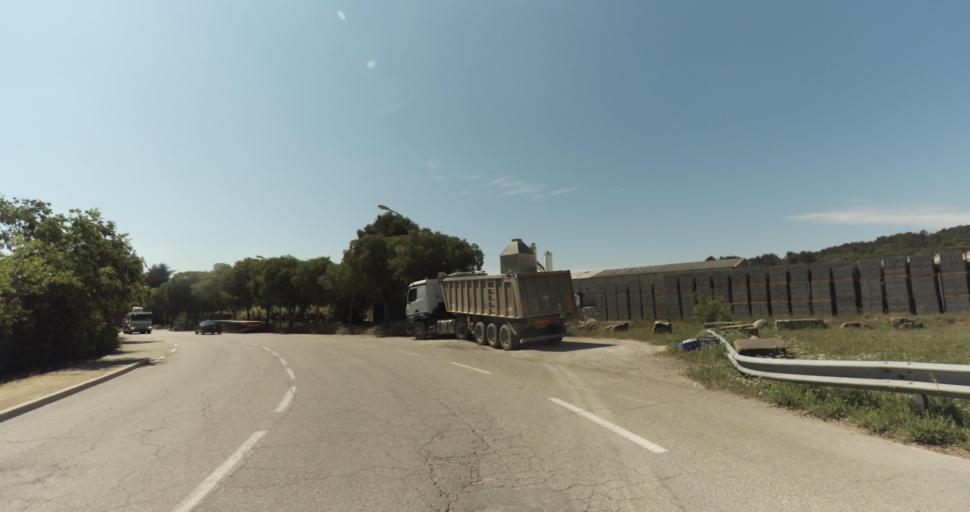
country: FR
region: Languedoc-Roussillon
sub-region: Departement du Gard
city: Milhaud
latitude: 43.8116
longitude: 4.3080
